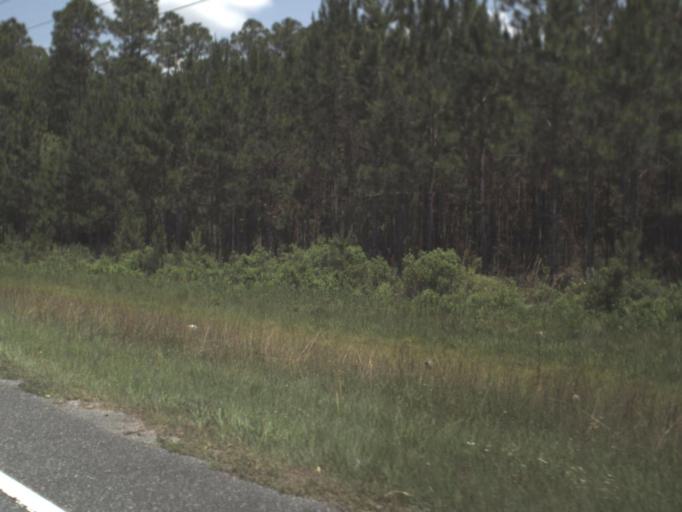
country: US
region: Florida
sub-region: Union County
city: Lake Butler
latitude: 29.9776
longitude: -82.2288
